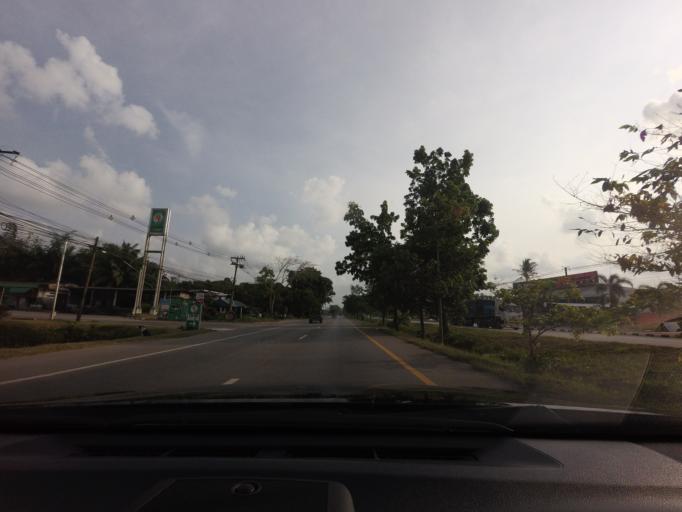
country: TH
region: Chumphon
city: Thung Tako
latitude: 10.1314
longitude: 99.0913
